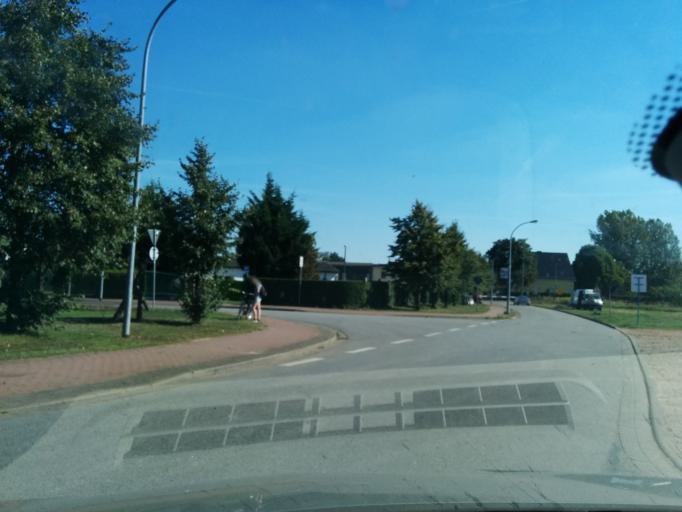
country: DE
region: Mecklenburg-Vorpommern
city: Torgelow
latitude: 53.6328
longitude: 14.0009
